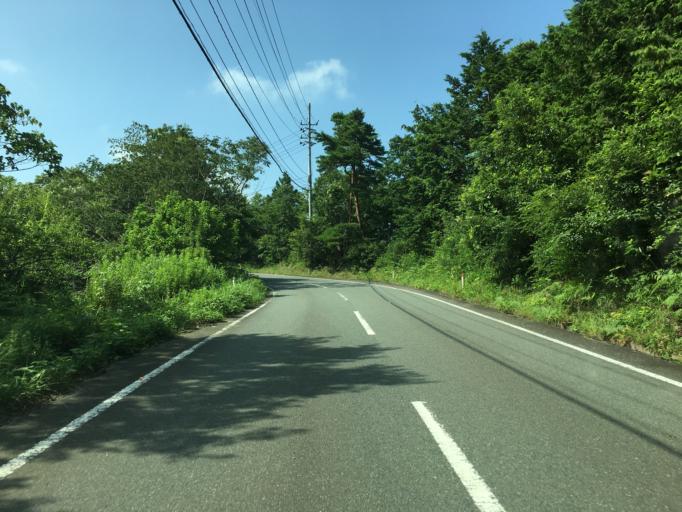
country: JP
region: Miyagi
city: Marumori
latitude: 37.8949
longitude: 140.8901
